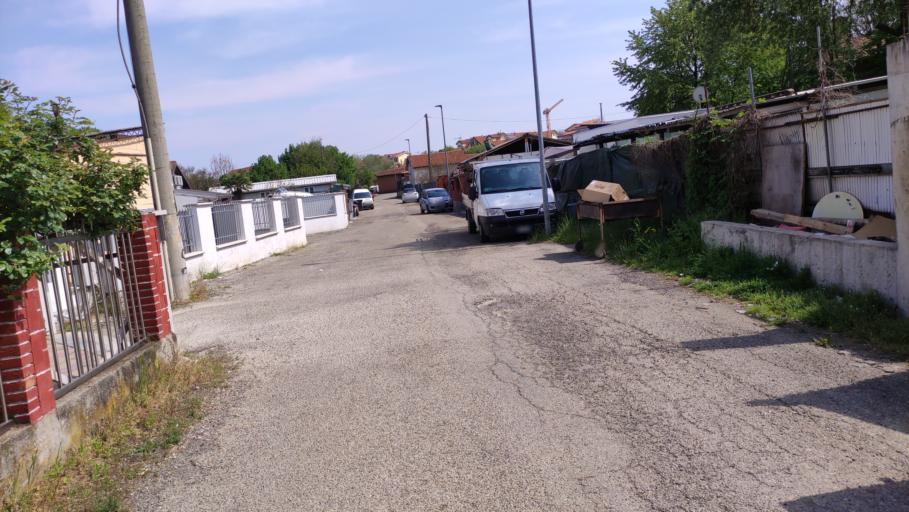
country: IT
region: Piedmont
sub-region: Provincia di Torino
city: Nichelino
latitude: 45.0063
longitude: 7.6424
